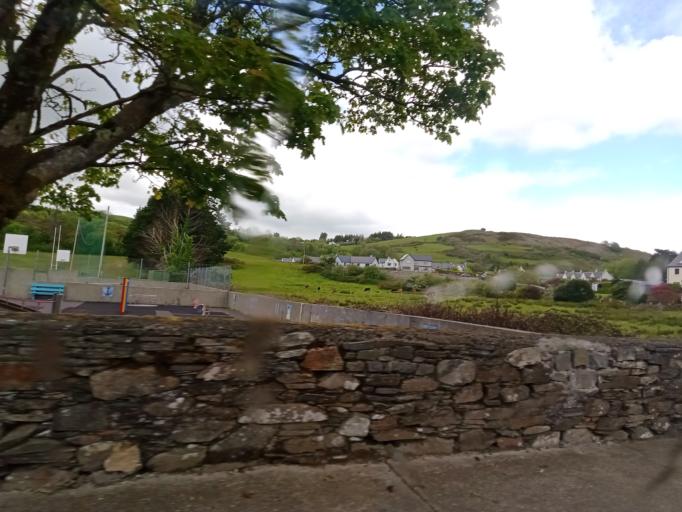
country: IE
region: Munster
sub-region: County Cork
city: Derry
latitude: 51.5551
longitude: -9.1446
